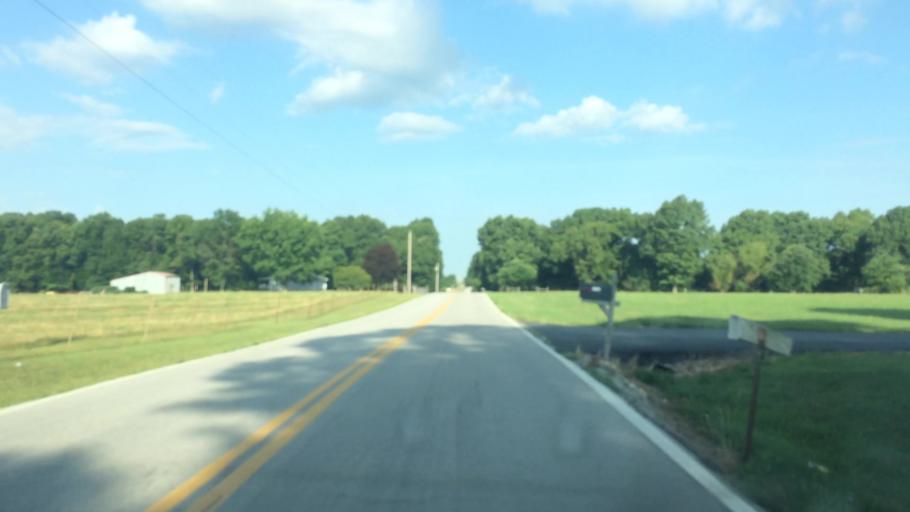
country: US
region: Missouri
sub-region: Greene County
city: Strafford
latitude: 37.2722
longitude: -93.1985
